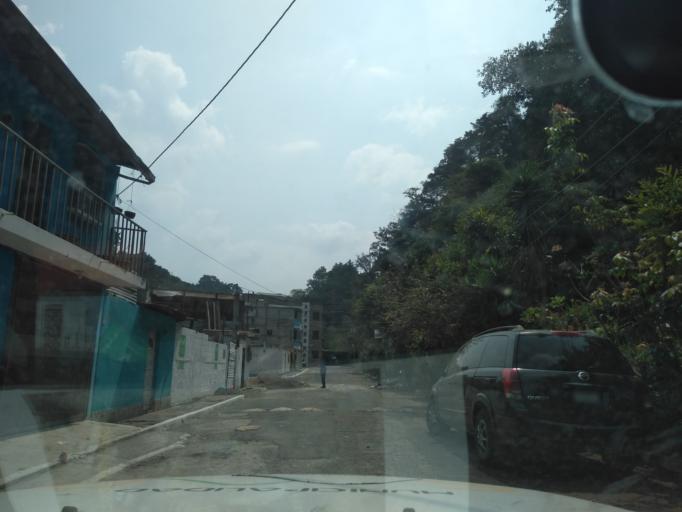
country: GT
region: Guatemala
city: Petapa
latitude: 14.5169
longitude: -90.5406
